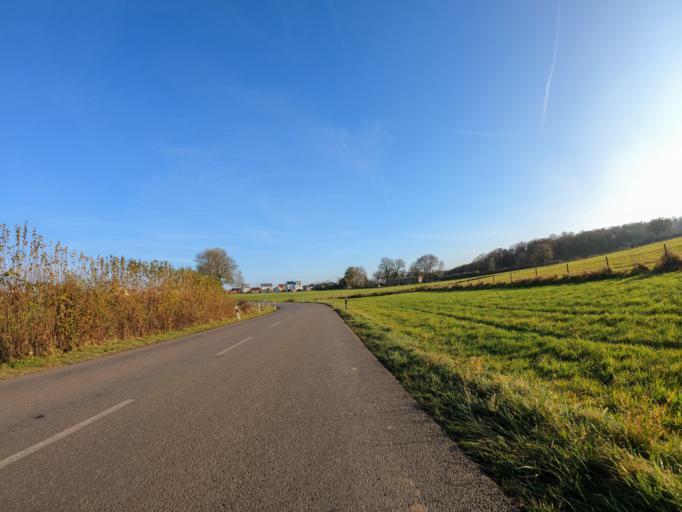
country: LU
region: Luxembourg
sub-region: Canton de Capellen
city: Garnich
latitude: 49.5991
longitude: 5.9388
